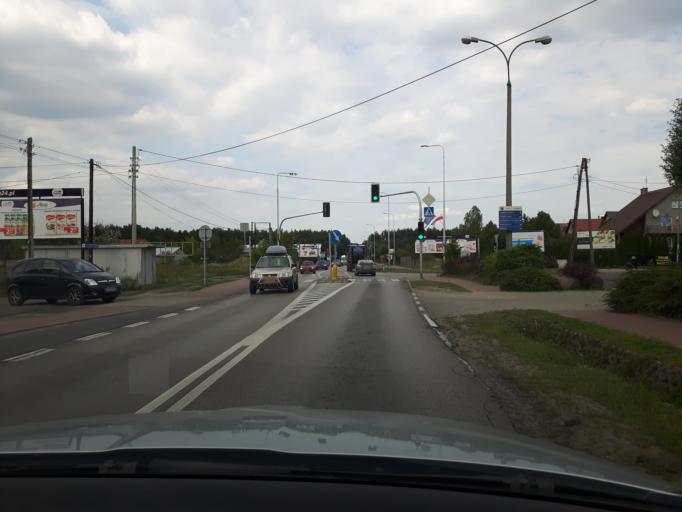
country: PL
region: Masovian Voivodeship
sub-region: Powiat legionowski
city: Stanislawow Pierwszy
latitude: 52.3972
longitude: 21.0352
